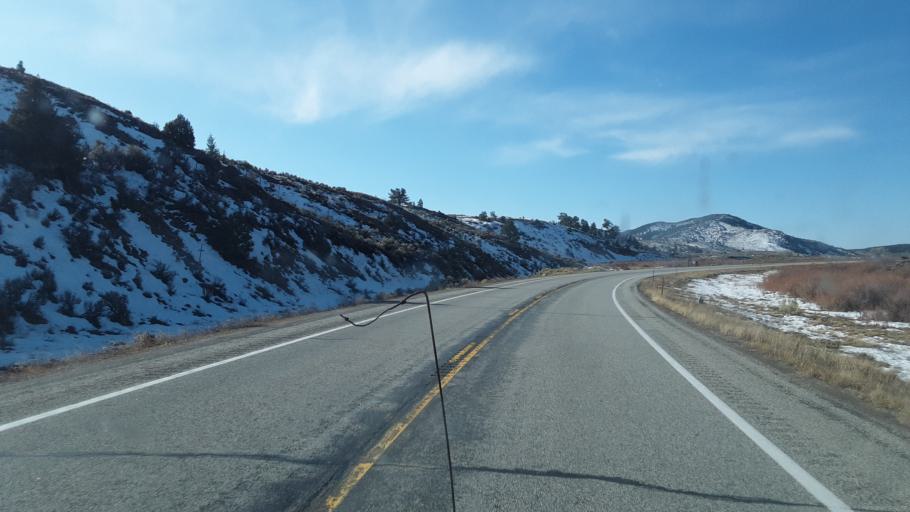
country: US
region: Colorado
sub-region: Costilla County
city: San Luis
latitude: 37.5175
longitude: -105.3007
